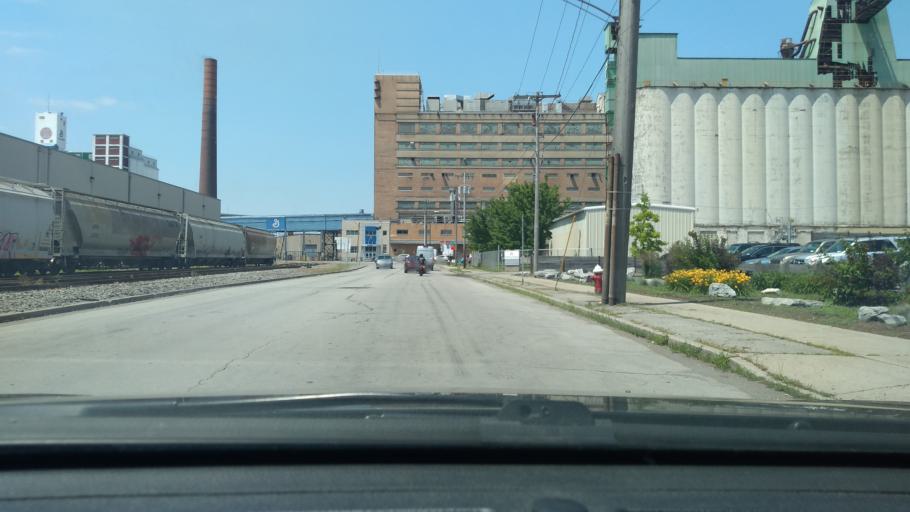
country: US
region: New York
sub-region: Erie County
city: Buffalo
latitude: 42.8697
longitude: -78.8738
